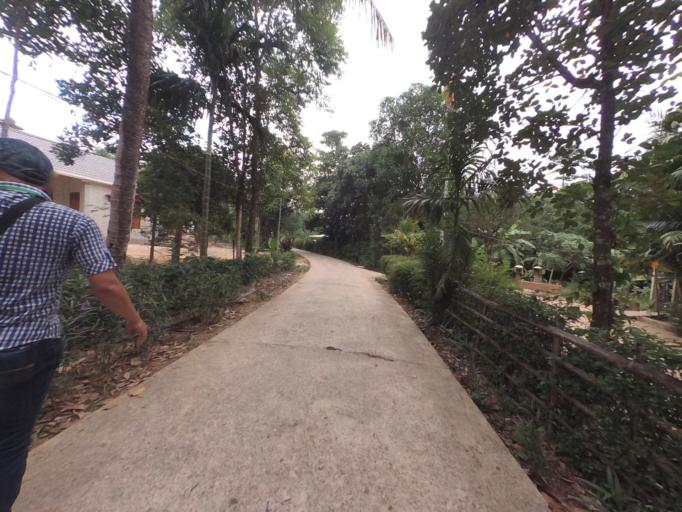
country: VN
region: Thua Thien-Hue
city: A Luoi
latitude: 16.2981
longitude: 107.3485
